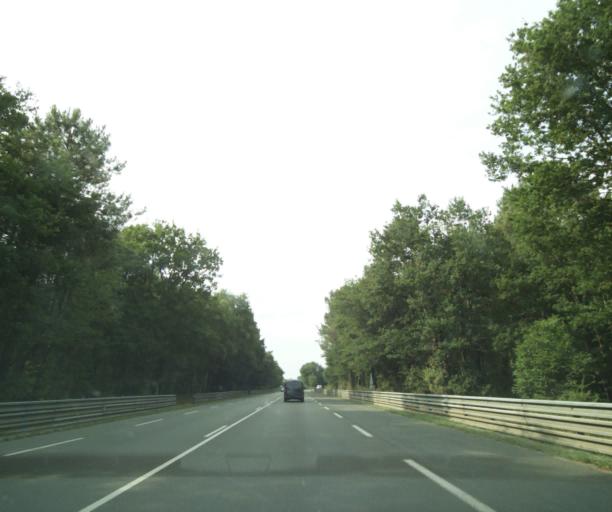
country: FR
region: Pays de la Loire
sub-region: Departement de la Sarthe
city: Mulsanne
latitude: 47.9373
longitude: 0.2370
